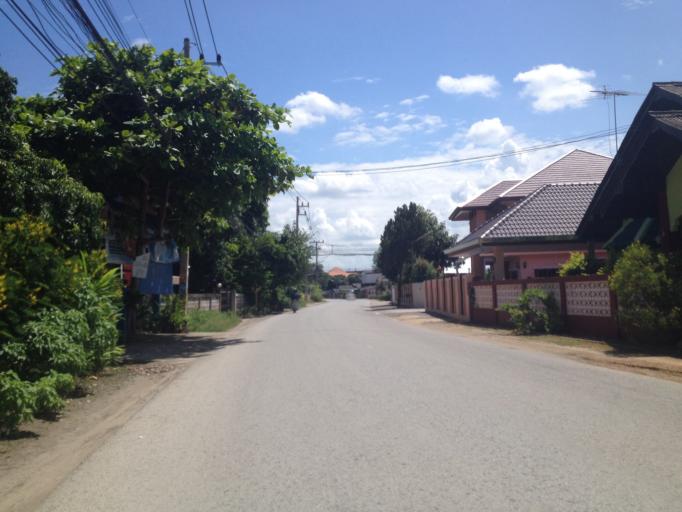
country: TH
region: Chiang Mai
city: Hang Dong
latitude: 18.6541
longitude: 98.9231
